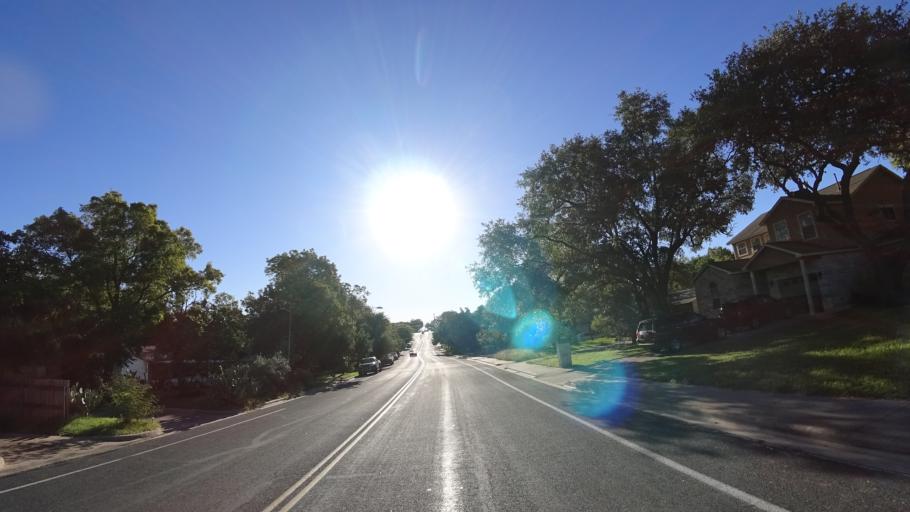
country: US
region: Texas
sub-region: Travis County
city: Austin
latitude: 30.2309
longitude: -97.7630
